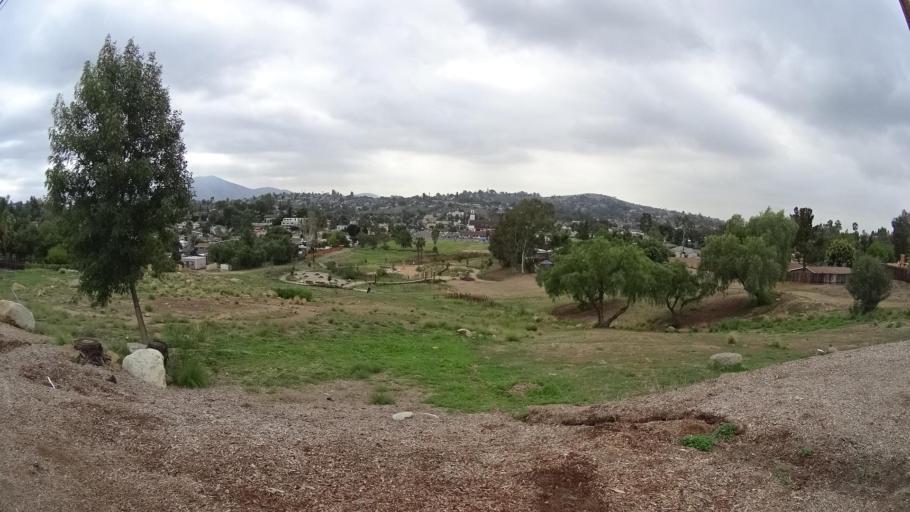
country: US
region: California
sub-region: San Diego County
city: Spring Valley
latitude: 32.7539
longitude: -116.9849
